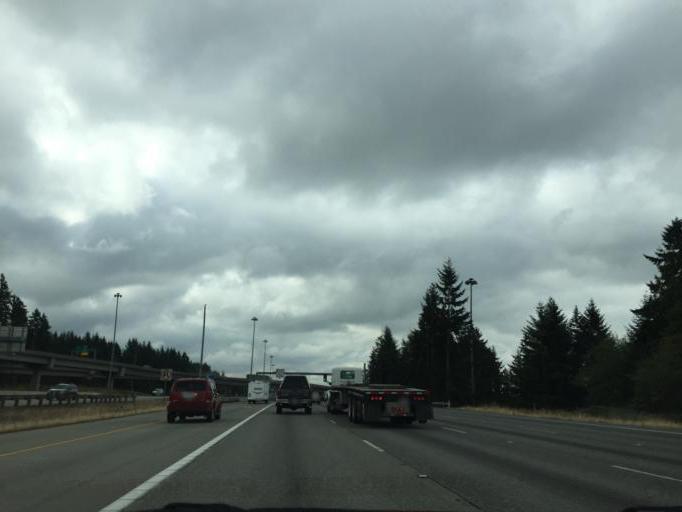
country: US
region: Washington
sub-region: King County
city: Lakeland South
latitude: 47.2909
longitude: -122.3064
